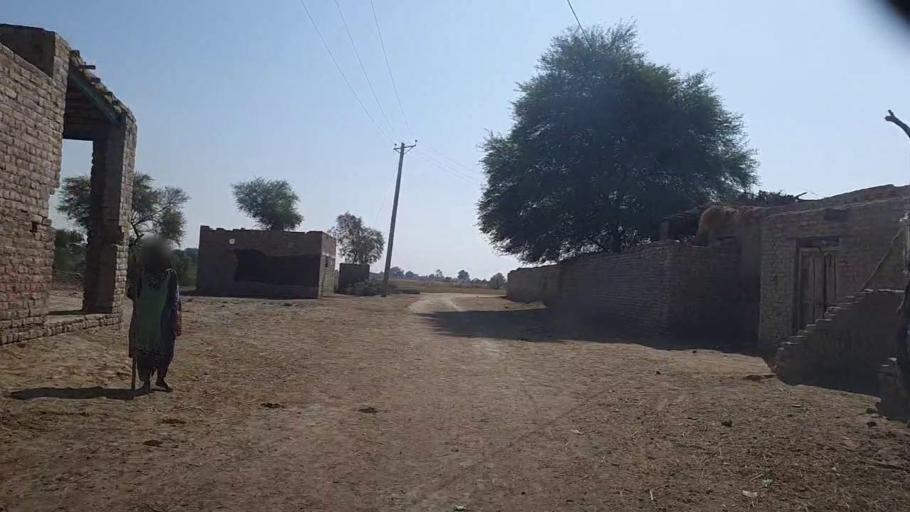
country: PK
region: Sindh
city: Thul
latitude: 28.1719
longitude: 68.7690
